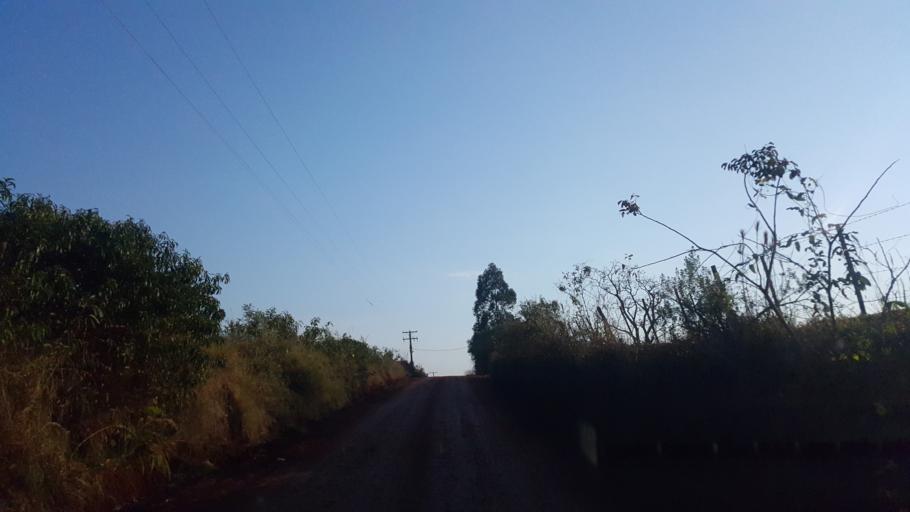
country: AR
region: Misiones
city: Capiovi
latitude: -26.9080
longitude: -55.0507
